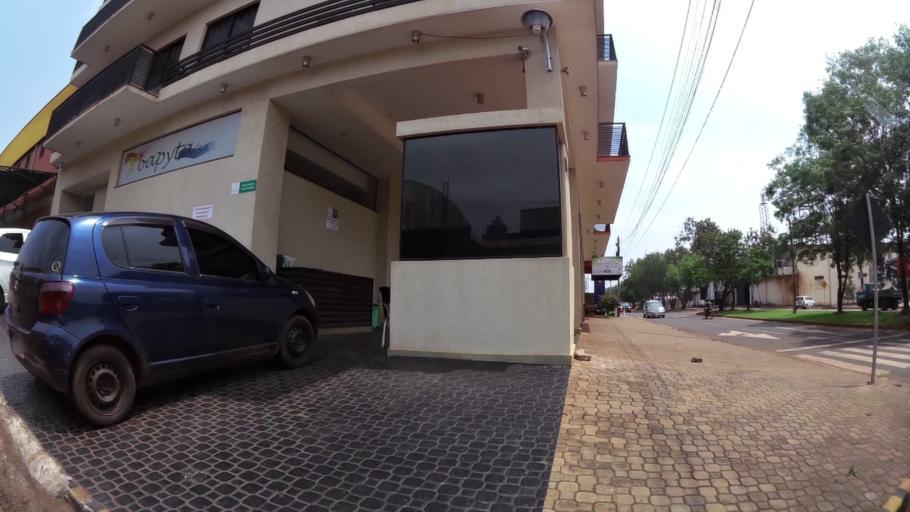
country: PY
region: Alto Parana
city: Ciudad del Este
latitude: -25.4990
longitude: -54.6317
